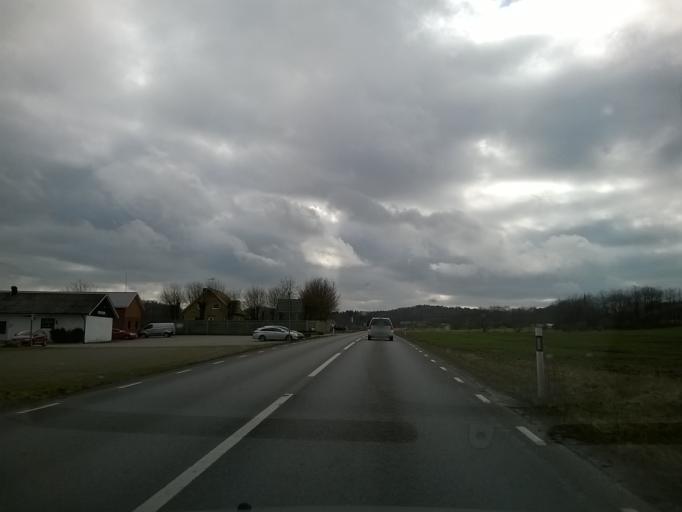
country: SE
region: Halland
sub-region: Varbergs Kommun
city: Tvaaker
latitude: 57.1373
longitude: 12.3969
